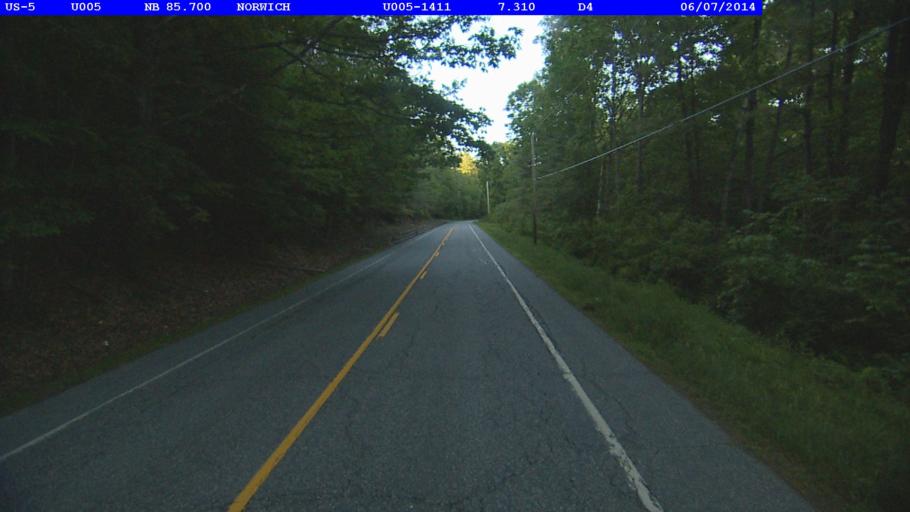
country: US
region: New Hampshire
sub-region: Grafton County
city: Lyme
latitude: 43.7629
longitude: -72.2218
